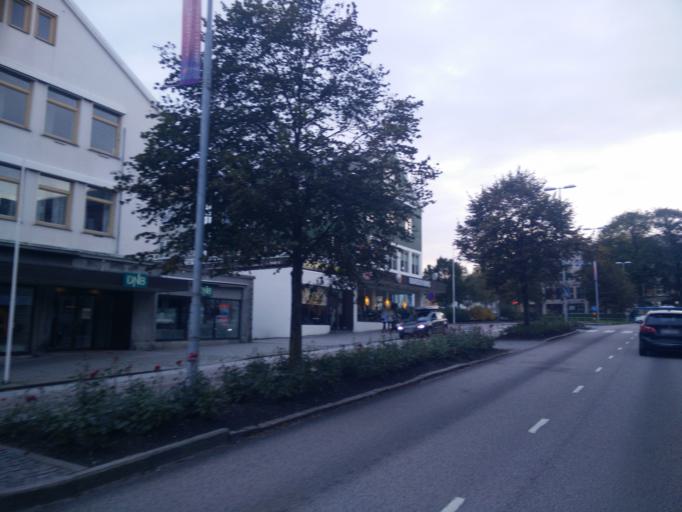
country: NO
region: More og Romsdal
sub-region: Kristiansund
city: Kristiansund
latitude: 63.1109
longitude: 7.7302
